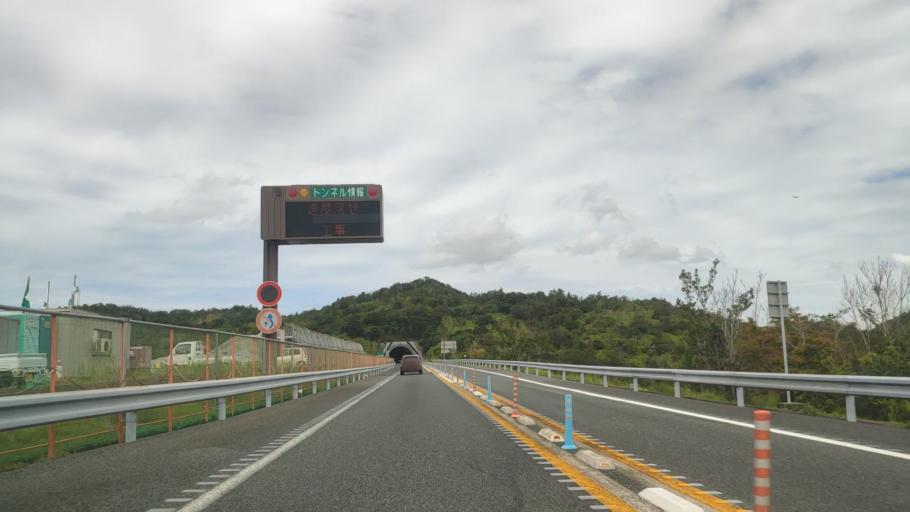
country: JP
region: Wakayama
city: Gobo
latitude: 33.8737
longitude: 135.1880
